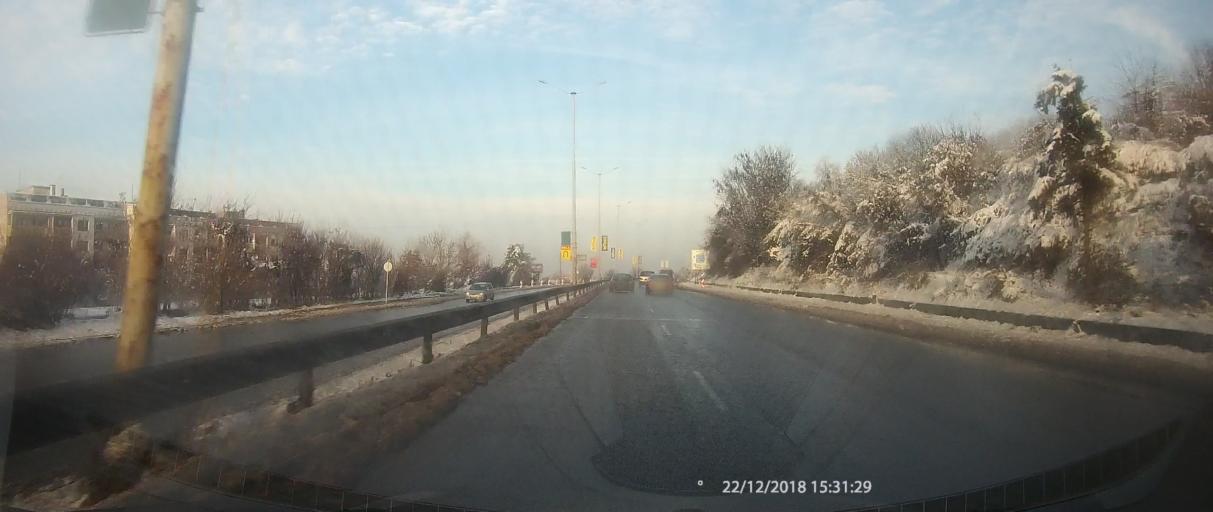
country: BG
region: Ruse
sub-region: Obshtina Ruse
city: Ruse
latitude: 43.8372
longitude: 25.9672
